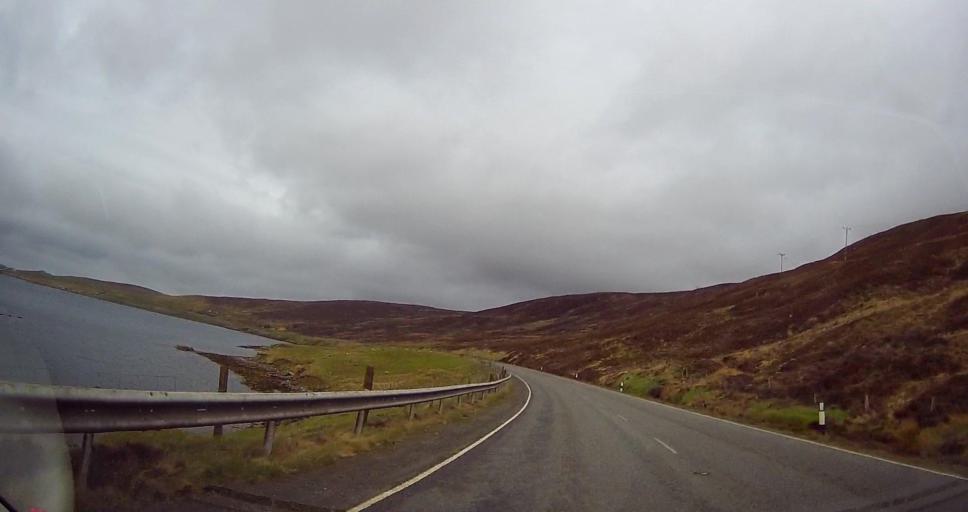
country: GB
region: Scotland
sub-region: Shetland Islands
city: Lerwick
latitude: 60.3623
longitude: -1.2862
